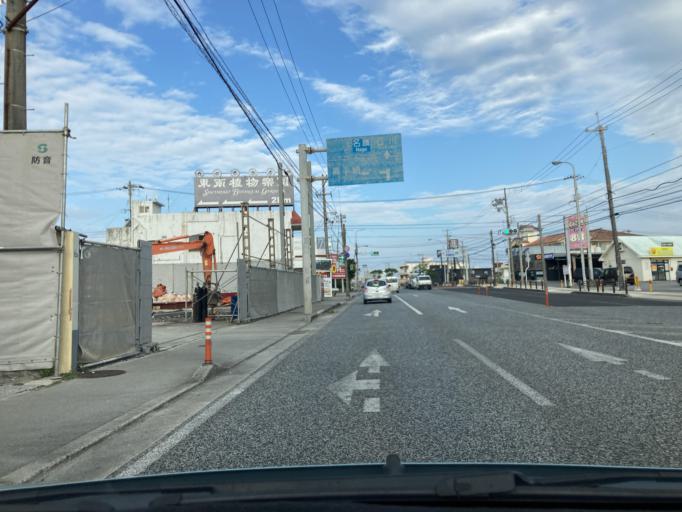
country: JP
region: Okinawa
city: Okinawa
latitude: 26.3668
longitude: 127.8165
